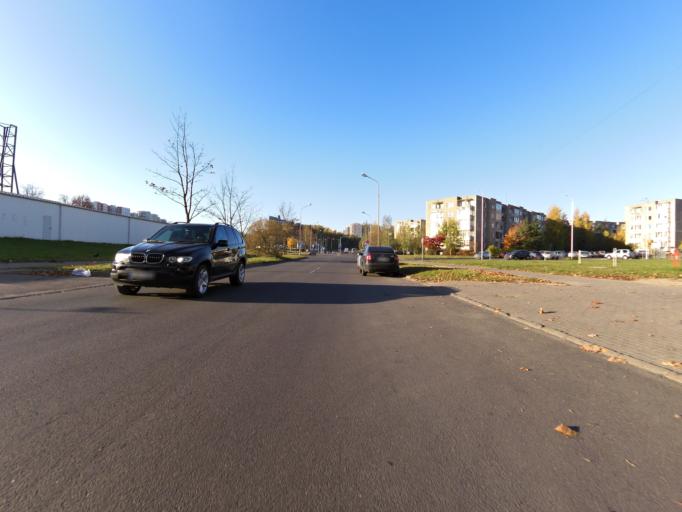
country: LT
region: Vilnius County
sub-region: Vilnius
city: Fabijoniskes
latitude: 54.7363
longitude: 25.2336
